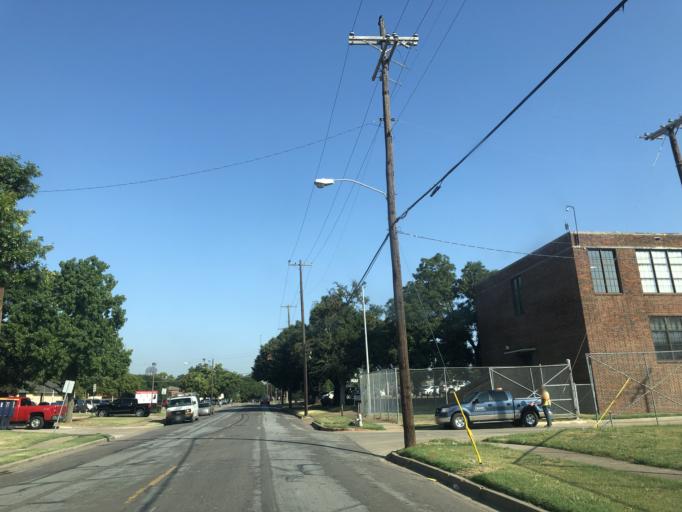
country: US
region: Texas
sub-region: Dallas County
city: Dallas
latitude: 32.7702
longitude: -96.7647
